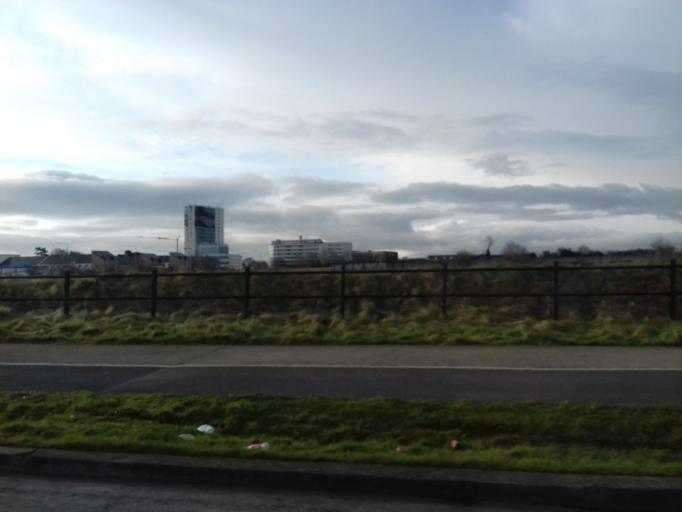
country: IE
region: Leinster
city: Ballymun
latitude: 53.4051
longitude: -6.2675
